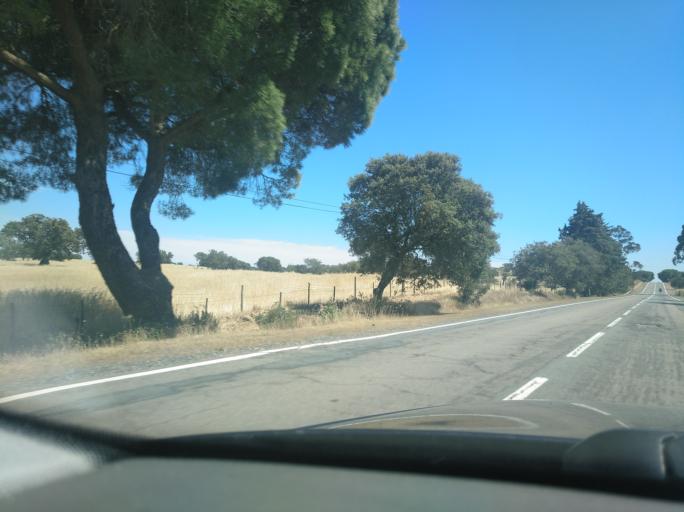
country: PT
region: Beja
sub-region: Almodovar
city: Almodovar
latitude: 37.5860
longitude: -8.0786
